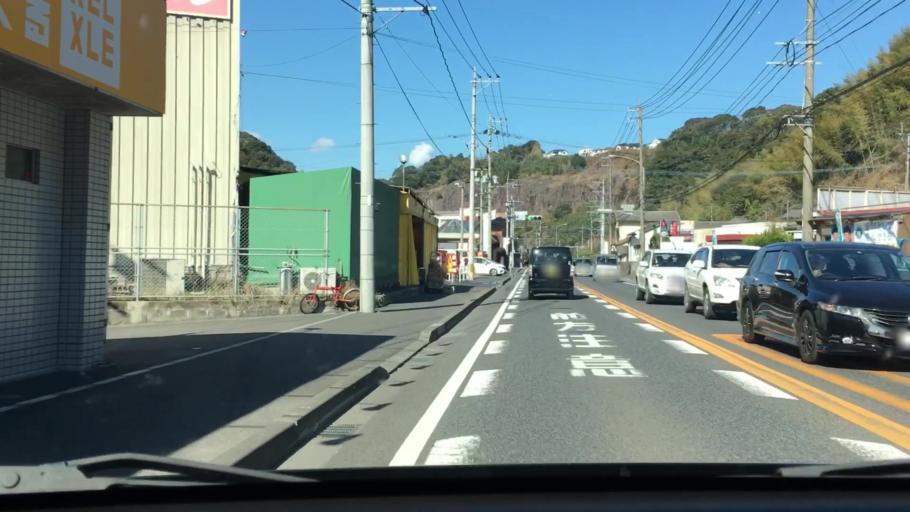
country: JP
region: Kagoshima
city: Kagoshima-shi
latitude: 31.6298
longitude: 130.5247
